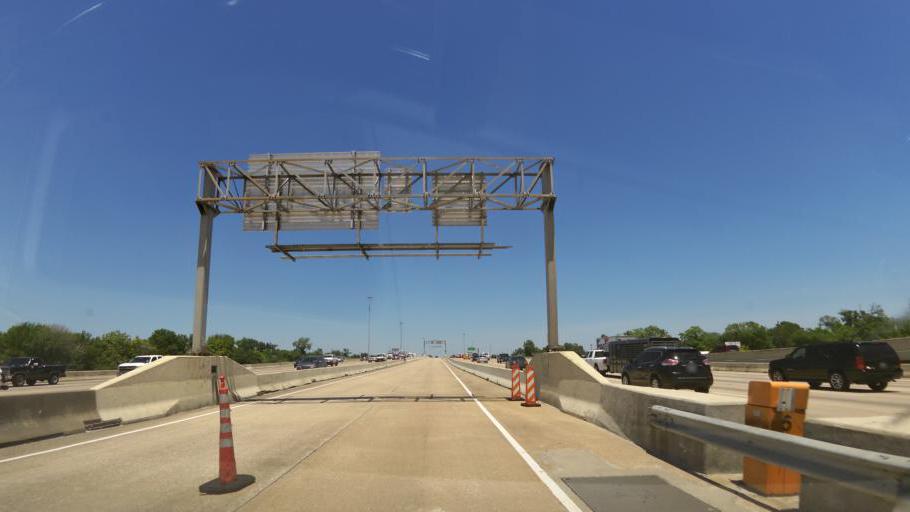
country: US
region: Texas
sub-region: Harris County
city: Aldine
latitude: 29.8562
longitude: -95.3336
